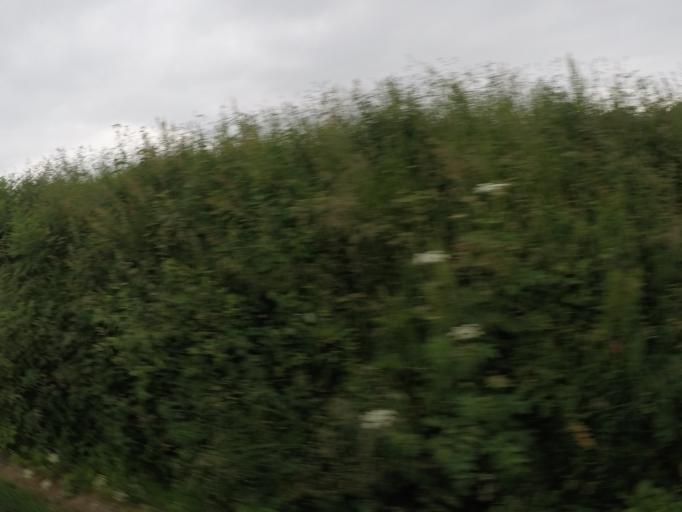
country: FR
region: Brittany
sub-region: Departement des Cotes-d'Armor
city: Goudelin
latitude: 48.6226
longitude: -3.0435
